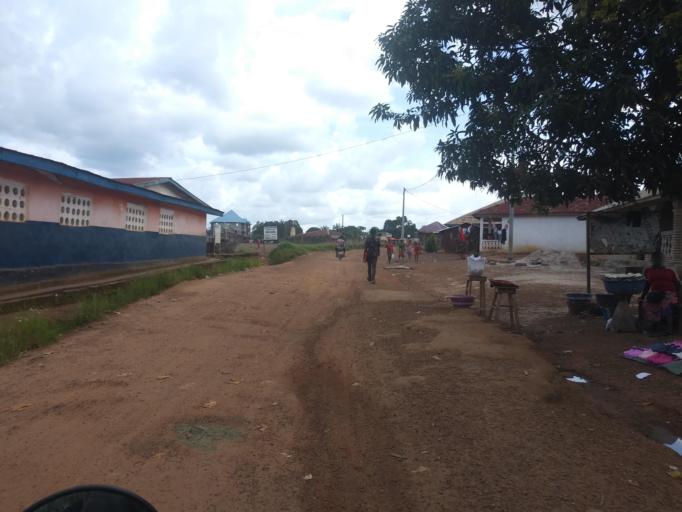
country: SL
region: Northern Province
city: Makeni
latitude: 8.8759
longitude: -12.0429
